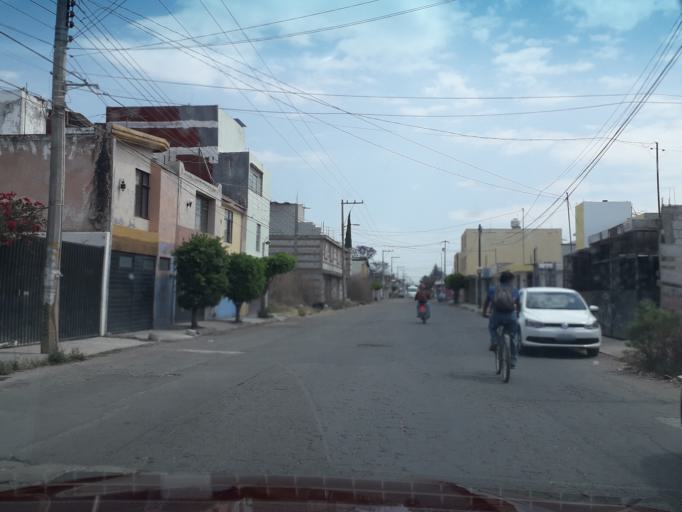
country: MX
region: Puebla
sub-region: Puebla
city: El Capulo (La Quebradora)
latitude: 18.9679
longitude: -98.2608
